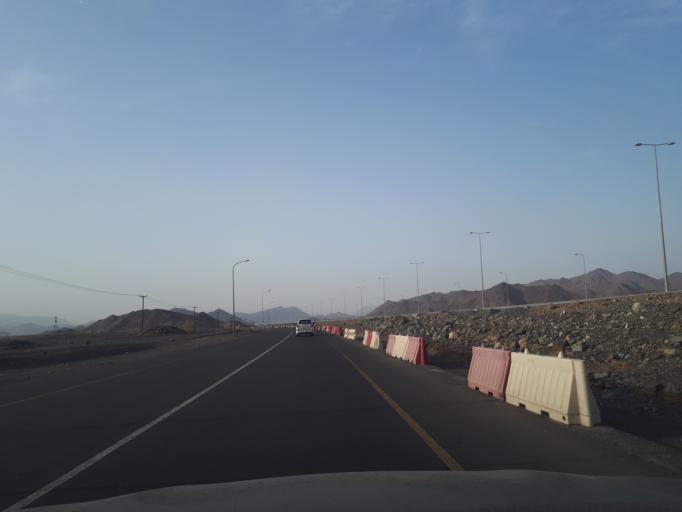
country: OM
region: Muhafazat ad Dakhiliyah
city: Sufalat Sama'il
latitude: 23.2773
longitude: 58.1065
